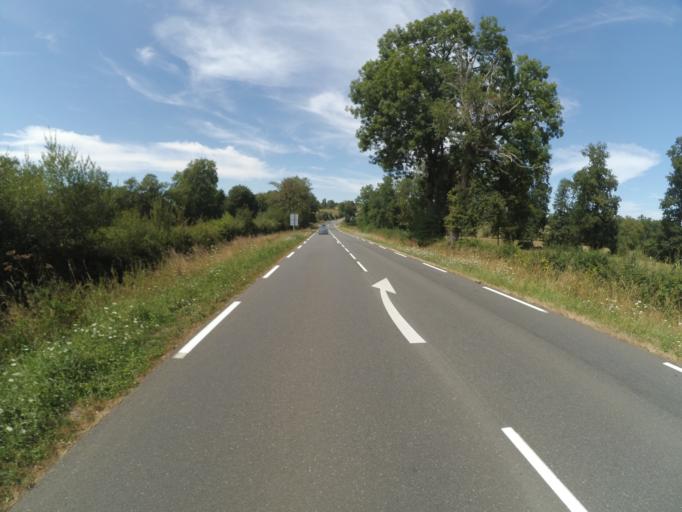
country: FR
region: Poitou-Charentes
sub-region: Departement de la Charente
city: Etagnac
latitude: 45.9270
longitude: 0.7400
